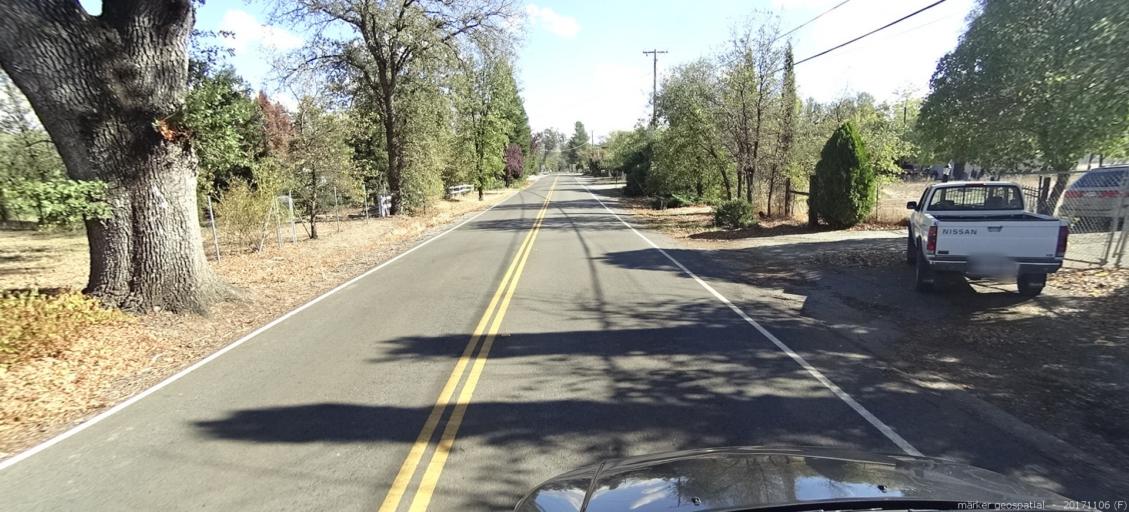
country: US
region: California
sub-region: Shasta County
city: Palo Cedro
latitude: 40.5928
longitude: -122.2338
